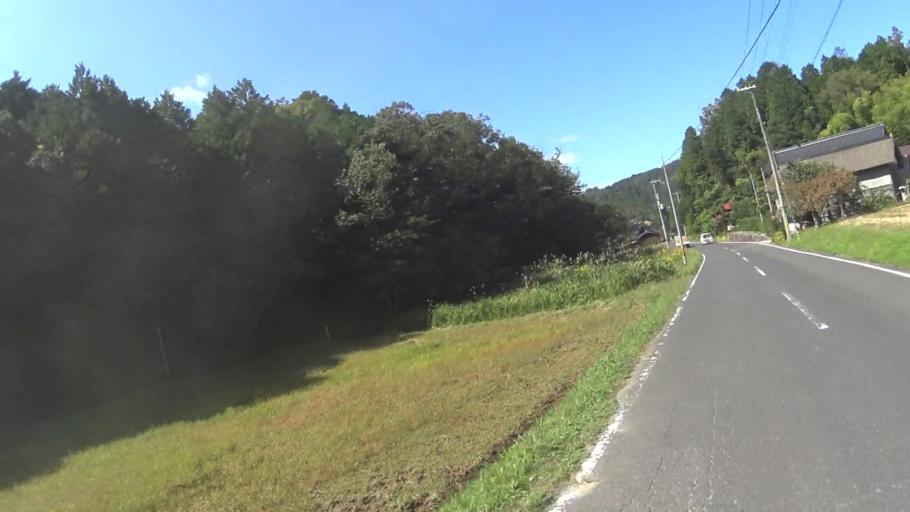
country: JP
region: Hyogo
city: Toyooka
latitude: 35.5944
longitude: 134.9492
